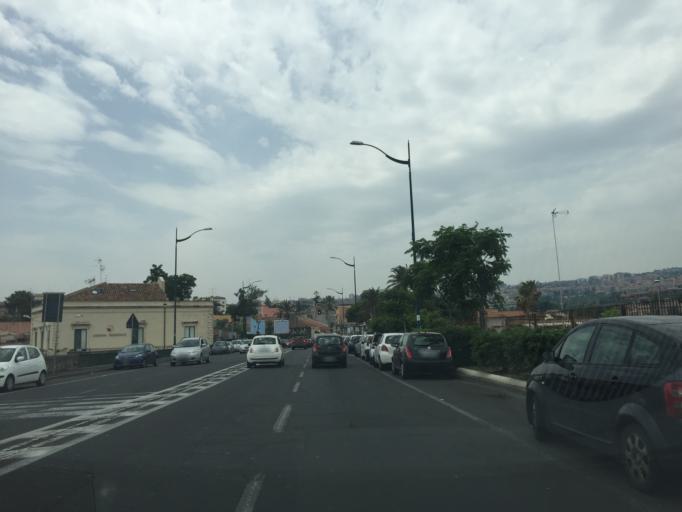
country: IT
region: Sicily
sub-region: Catania
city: Cerza
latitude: 37.5289
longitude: 15.1144
